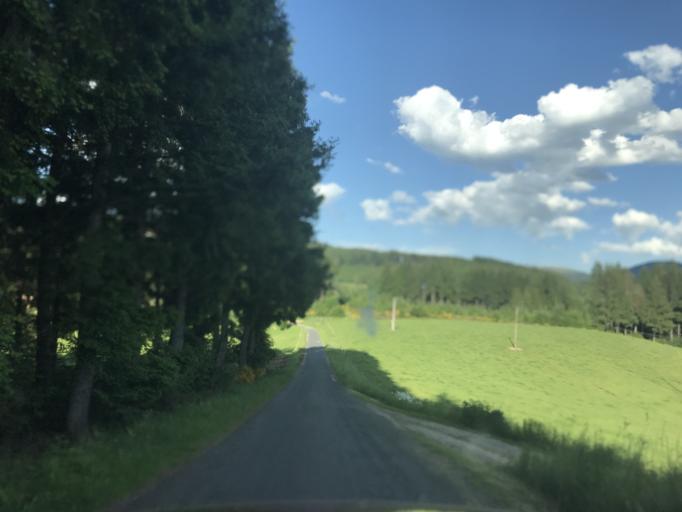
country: FR
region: Auvergne
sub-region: Departement du Puy-de-Dome
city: Job
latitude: 45.6778
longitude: 3.6900
